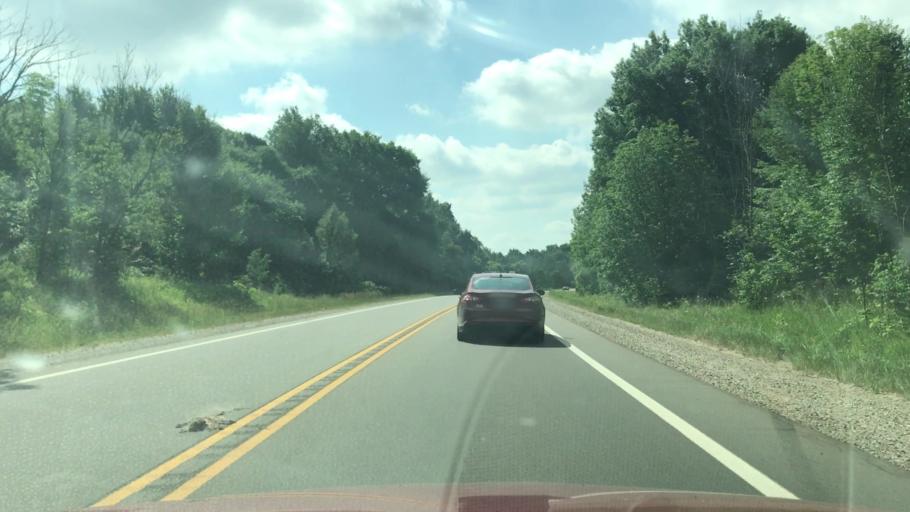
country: US
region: Michigan
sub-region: Kent County
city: Kent City
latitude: 43.1972
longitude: -85.7239
